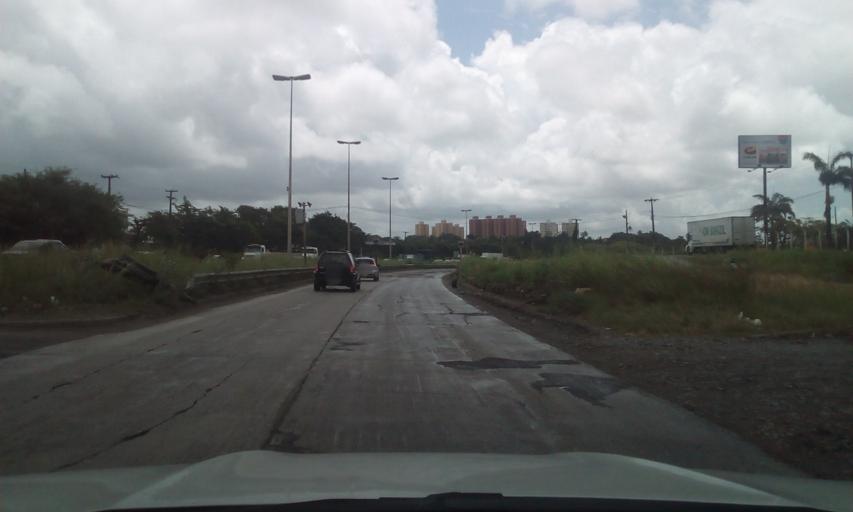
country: BR
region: Pernambuco
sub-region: Jaboatao Dos Guararapes
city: Jaboatao dos Guararapes
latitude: -8.0993
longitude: -34.9501
